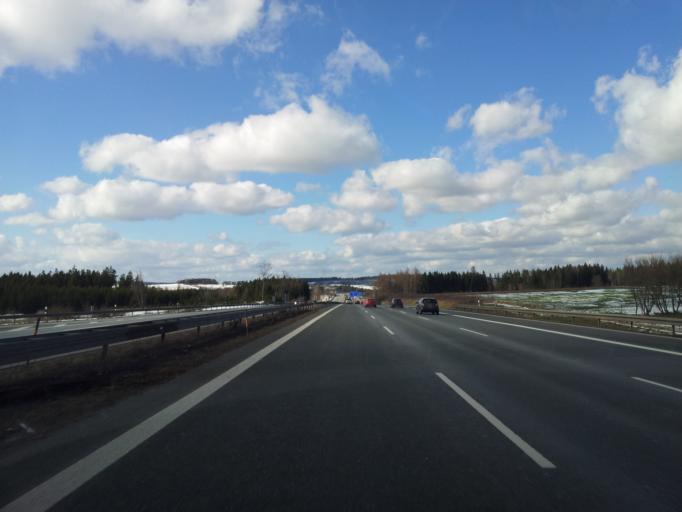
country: DE
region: Bavaria
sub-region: Upper Franconia
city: Leupoldsgrun
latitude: 50.3051
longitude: 11.8046
